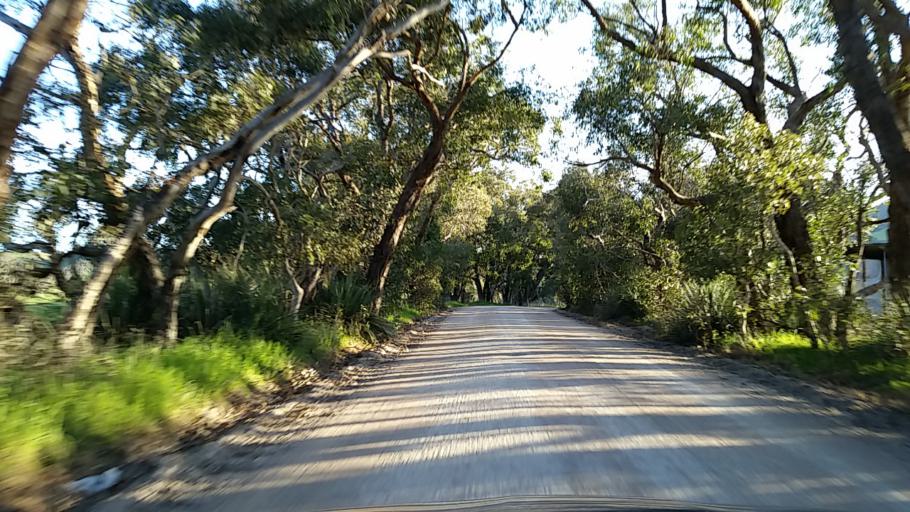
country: AU
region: South Australia
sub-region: Alexandrina
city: Mount Compass
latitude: -35.3136
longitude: 138.6705
